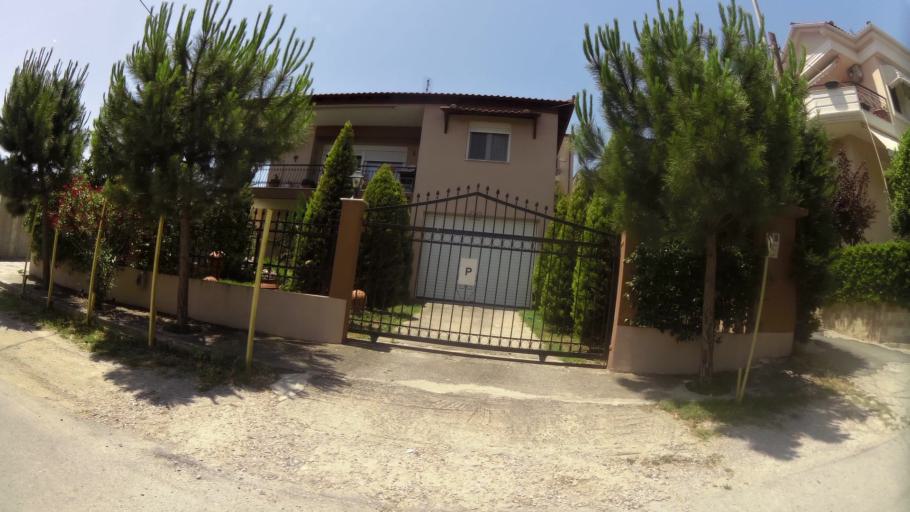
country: GR
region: Central Macedonia
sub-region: Nomos Thessalonikis
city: Plagiari
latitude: 40.4690
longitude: 22.9574
